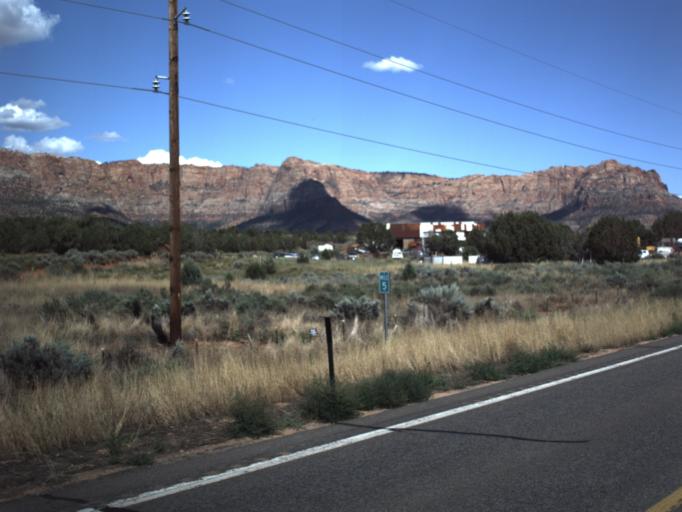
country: US
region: Arizona
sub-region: Mohave County
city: Colorado City
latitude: 37.0395
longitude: -113.0747
